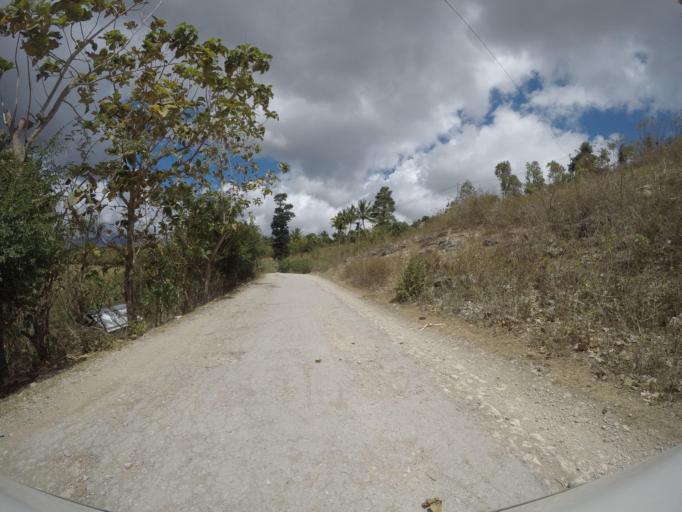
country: TL
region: Baucau
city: Baucau
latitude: -8.5173
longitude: 126.6900
